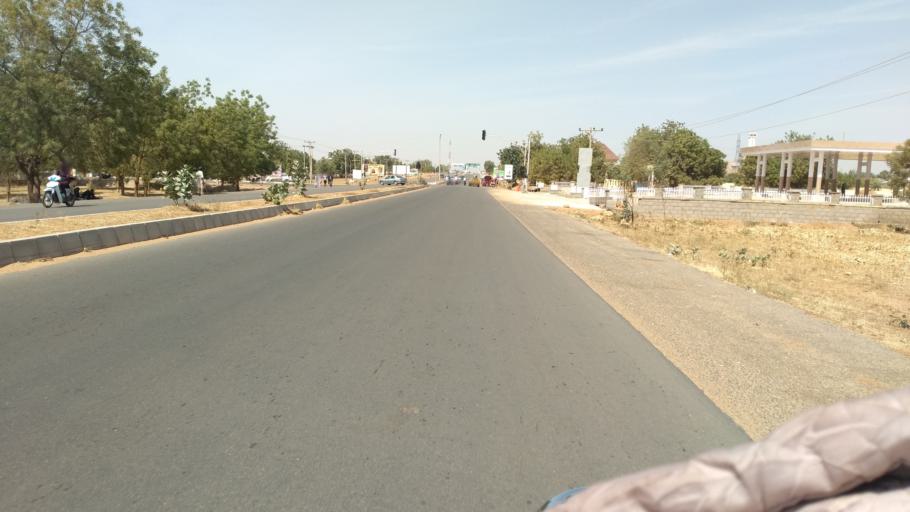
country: NG
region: Jigawa
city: Dutse
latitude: 11.6840
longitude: 9.3397
